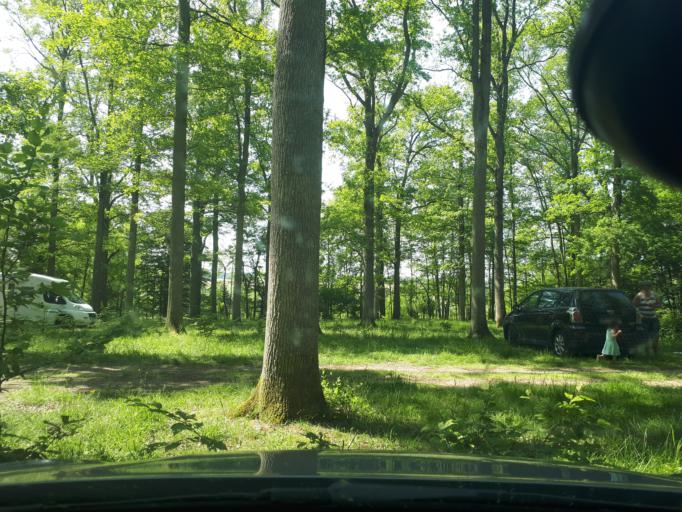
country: FR
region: Pays de la Loire
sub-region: Departement de la Sarthe
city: Le Breil-sur-Merize
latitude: 47.9947
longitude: 0.5004
